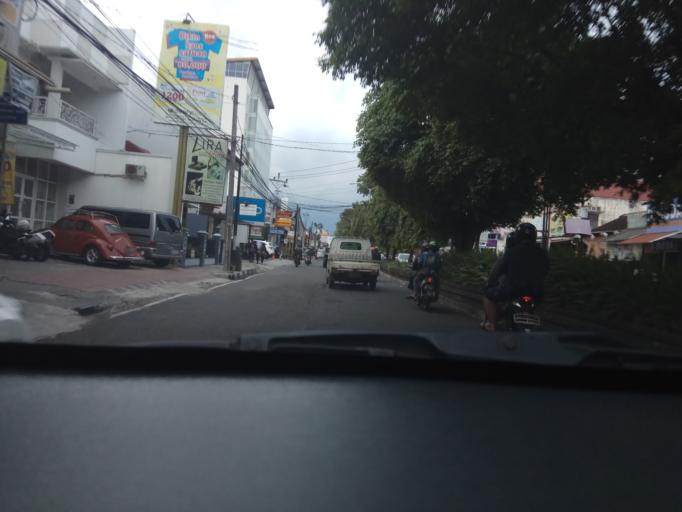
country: ID
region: Daerah Istimewa Yogyakarta
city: Yogyakarta
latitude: -7.7681
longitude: 110.3913
